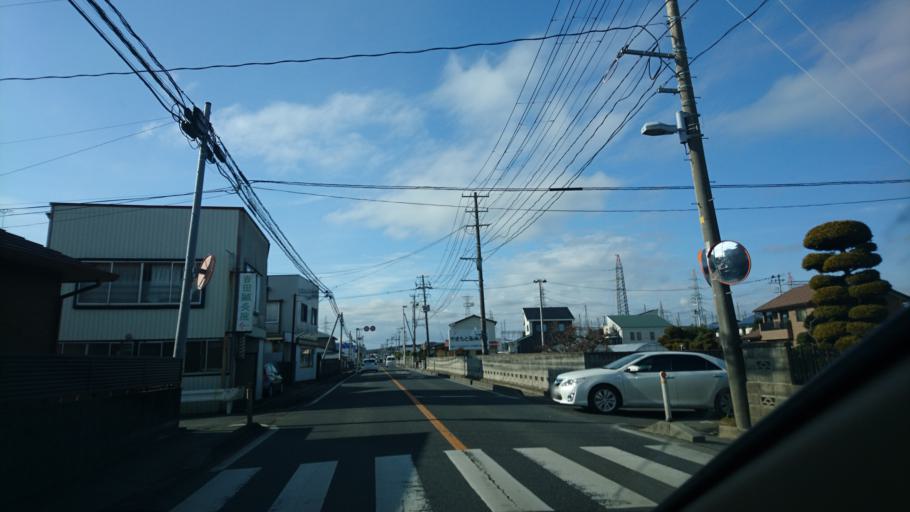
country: JP
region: Miyagi
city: Yamoto
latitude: 38.4725
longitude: 141.2221
